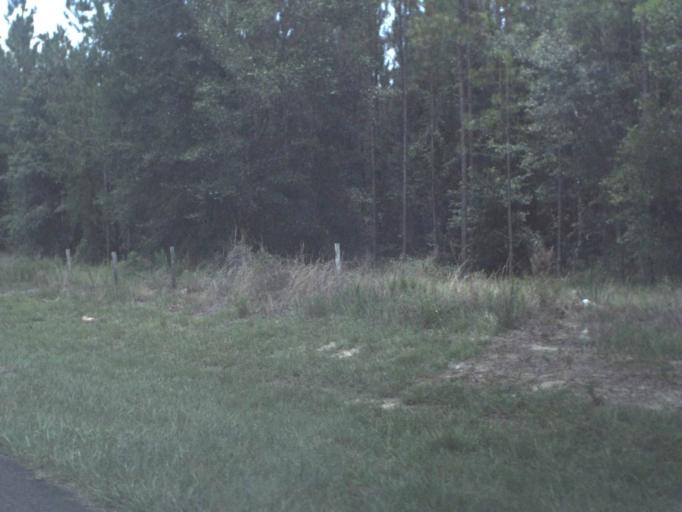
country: US
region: Florida
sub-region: Levy County
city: Williston
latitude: 29.4596
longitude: -82.4763
